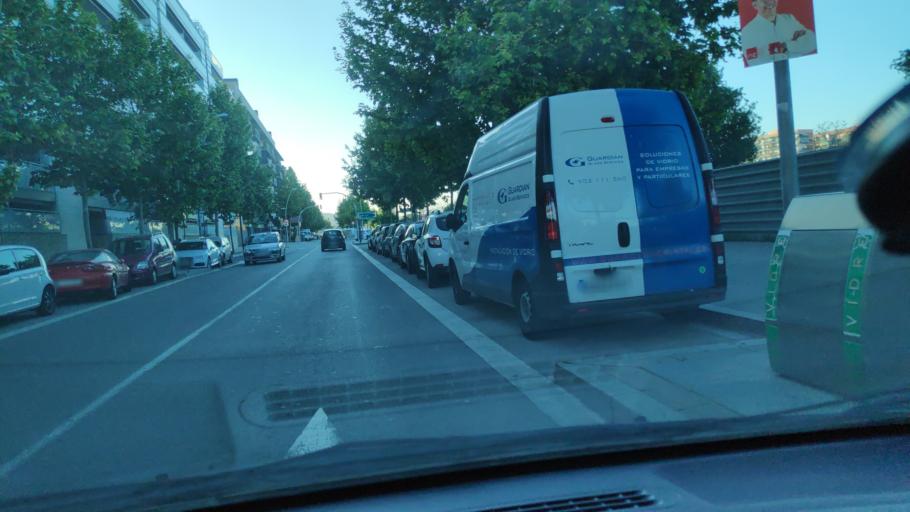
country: ES
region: Catalonia
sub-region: Provincia de Barcelona
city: Sant Adria de Besos
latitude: 41.4239
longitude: 2.2214
